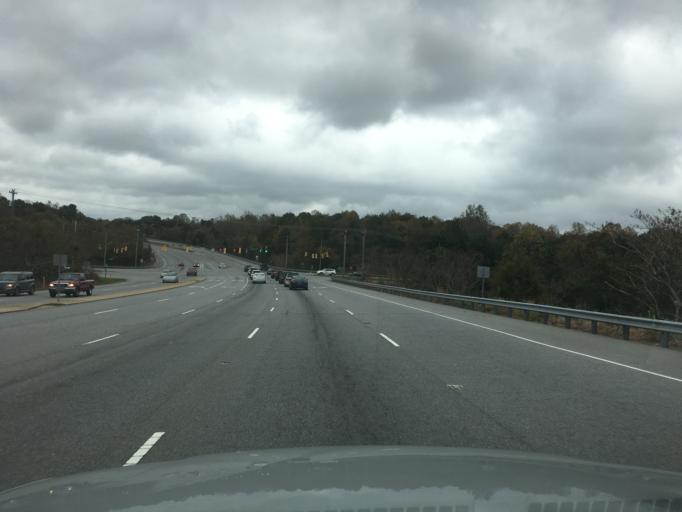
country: US
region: North Carolina
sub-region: Catawba County
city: Saint Stephens
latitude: 35.7250
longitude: -81.2917
